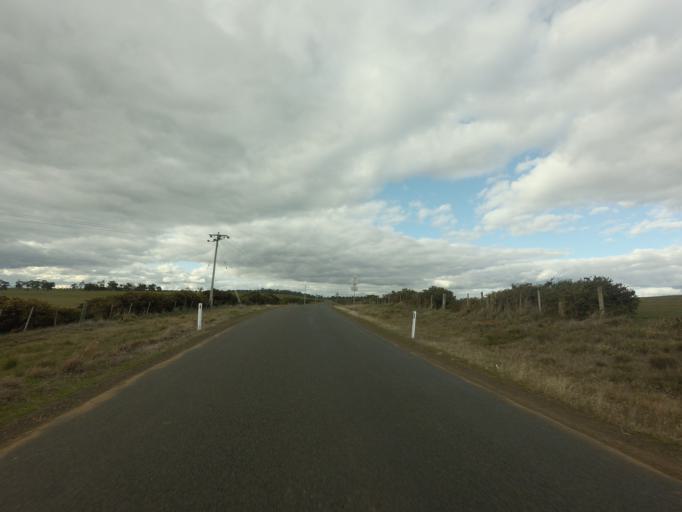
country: AU
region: Tasmania
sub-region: Northern Midlands
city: Evandale
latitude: -41.9064
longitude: 147.3935
